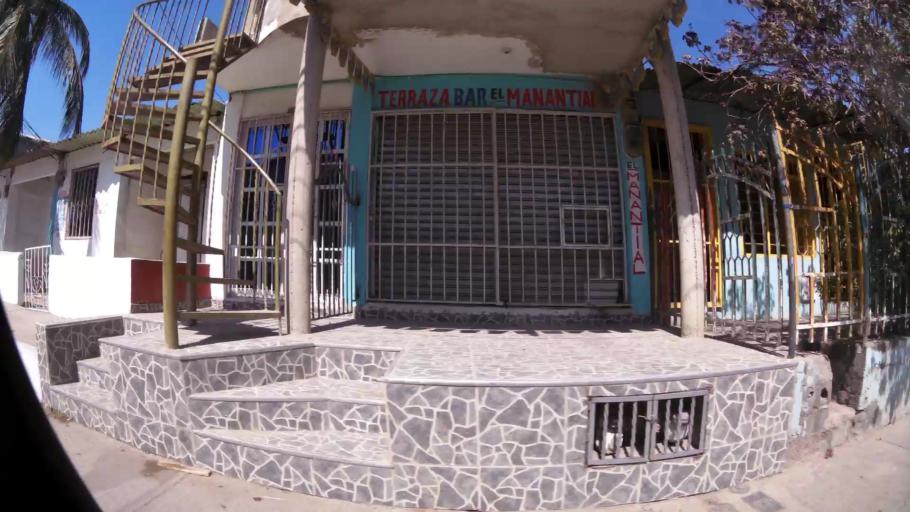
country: CO
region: Bolivar
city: Cartagena
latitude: 10.3870
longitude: -75.4562
